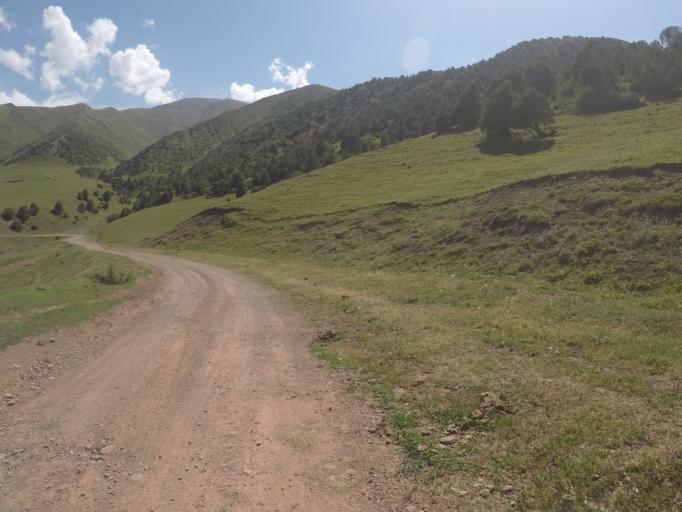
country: KG
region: Chuy
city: Bishkek
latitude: 42.6449
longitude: 74.5700
